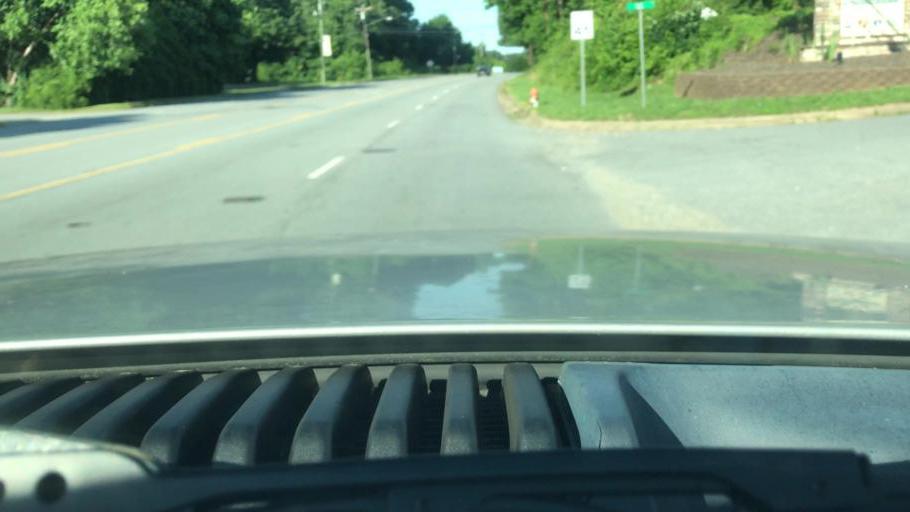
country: US
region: North Carolina
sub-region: Yadkin County
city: Jonesville
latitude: 36.2399
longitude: -80.8403
